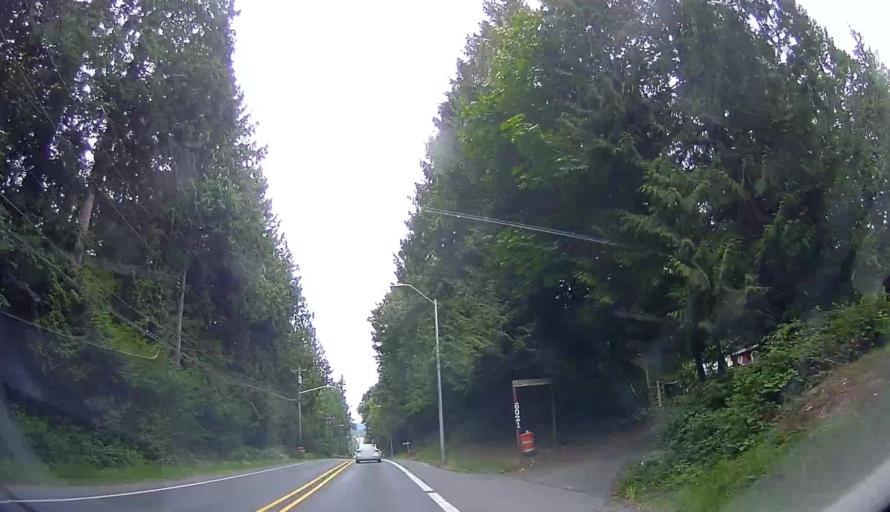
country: US
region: Washington
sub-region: Snohomish County
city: Tulalip
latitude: 48.0502
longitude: -122.2575
